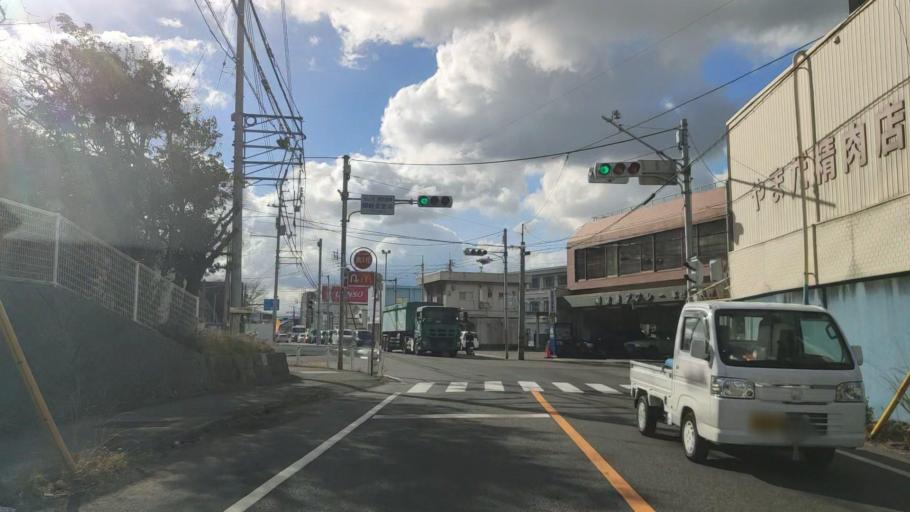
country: JP
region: Ehime
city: Masaki-cho
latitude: 33.8302
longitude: 132.7085
